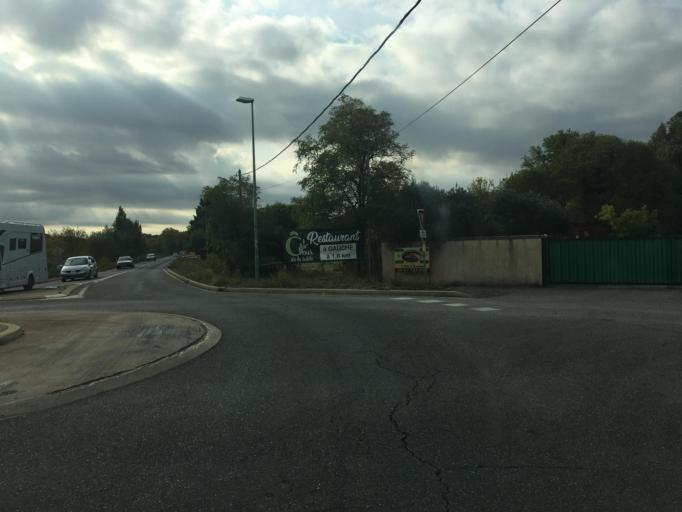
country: FR
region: Languedoc-Roussillon
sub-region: Departement de l'Herault
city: Nebian
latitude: 43.6019
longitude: 3.4392
